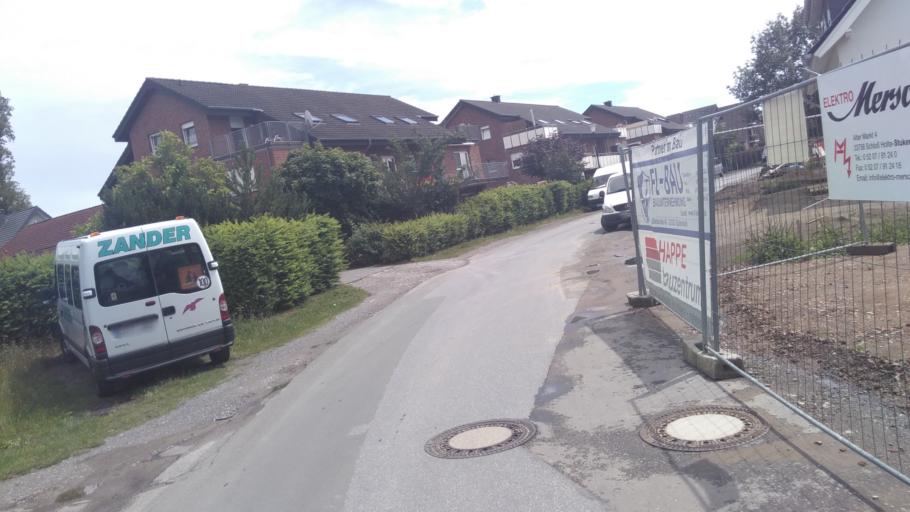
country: DE
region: North Rhine-Westphalia
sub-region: Regierungsbezirk Detmold
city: Verl
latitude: 51.8729
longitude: 8.4958
